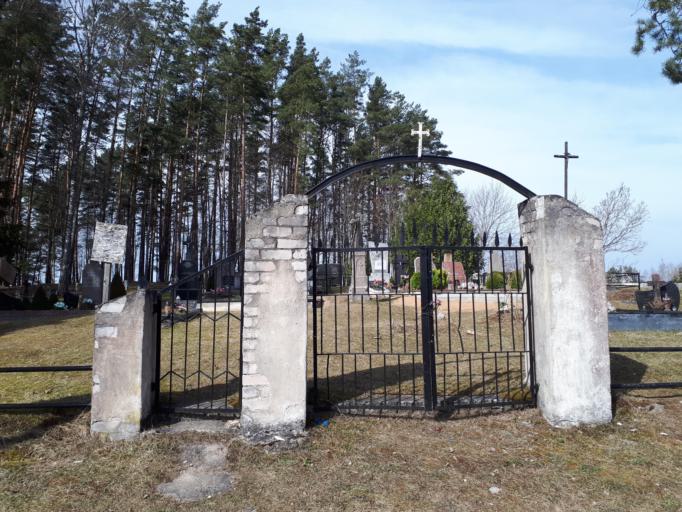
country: LT
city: Zarasai
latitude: 55.6244
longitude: 26.0875
